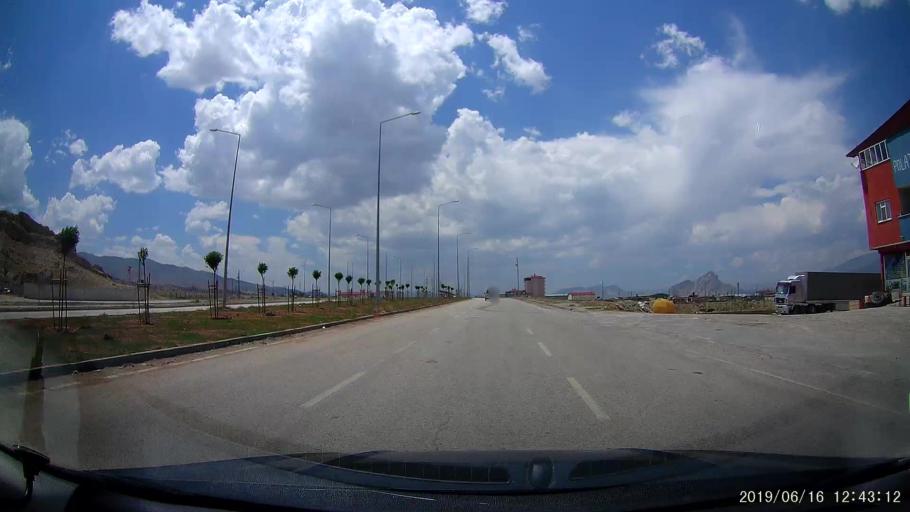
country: TR
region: Agri
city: Dogubayazit
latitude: 39.5584
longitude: 44.1205
